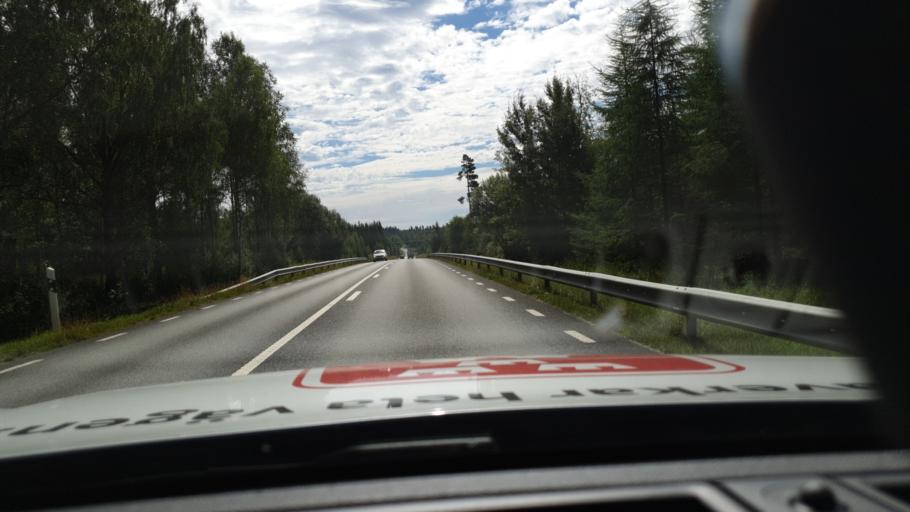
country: SE
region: Joenkoeping
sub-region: Savsjo Kommun
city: Vrigstad
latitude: 57.4184
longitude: 14.3347
